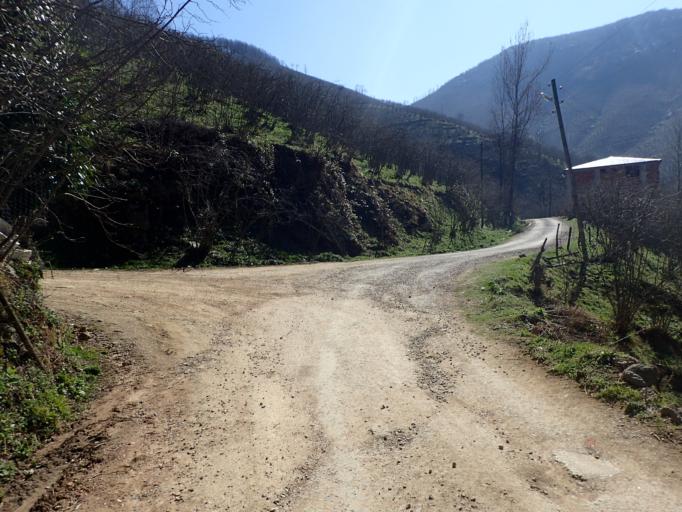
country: TR
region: Ordu
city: Catalpinar
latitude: 40.8643
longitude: 37.4936
